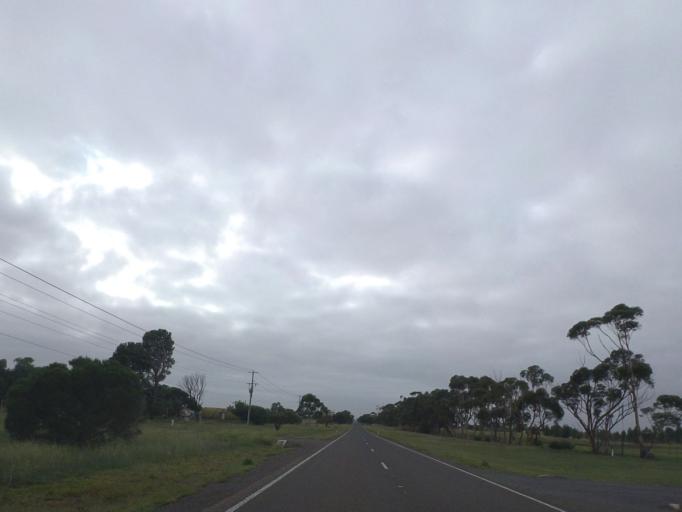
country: AU
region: Victoria
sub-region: Melton
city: Kurunjang
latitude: -37.7034
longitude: 144.6264
